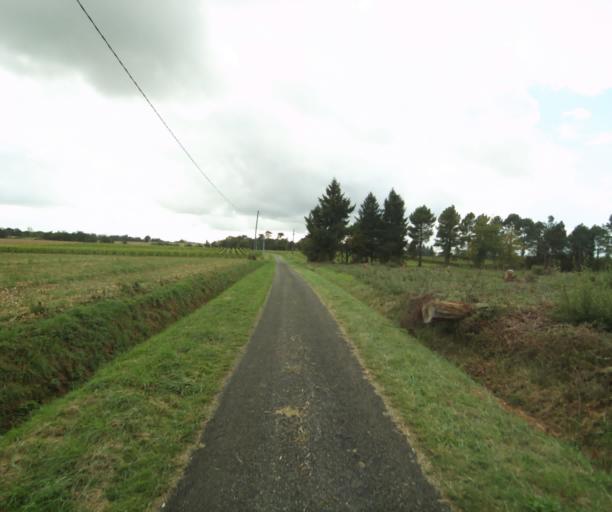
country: FR
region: Midi-Pyrenees
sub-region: Departement du Gers
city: Cazaubon
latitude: 43.8671
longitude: -0.0376
